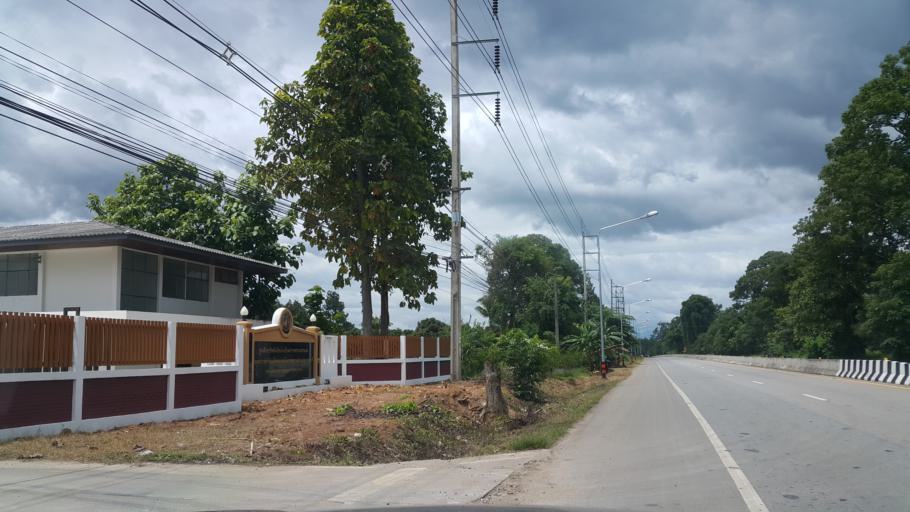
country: TH
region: Chiang Mai
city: Mae Taeng
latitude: 19.1683
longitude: 98.9486
